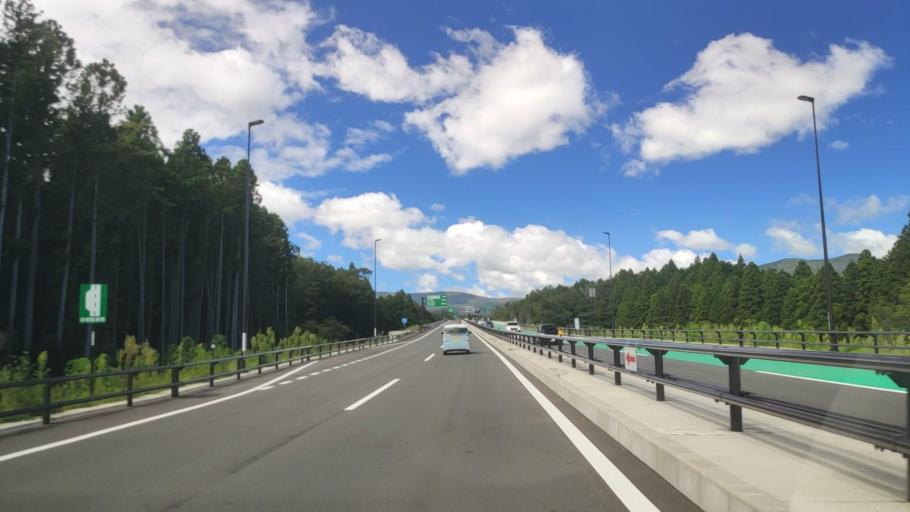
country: JP
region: Shizuoka
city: Gotemba
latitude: 35.3301
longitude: 138.8996
